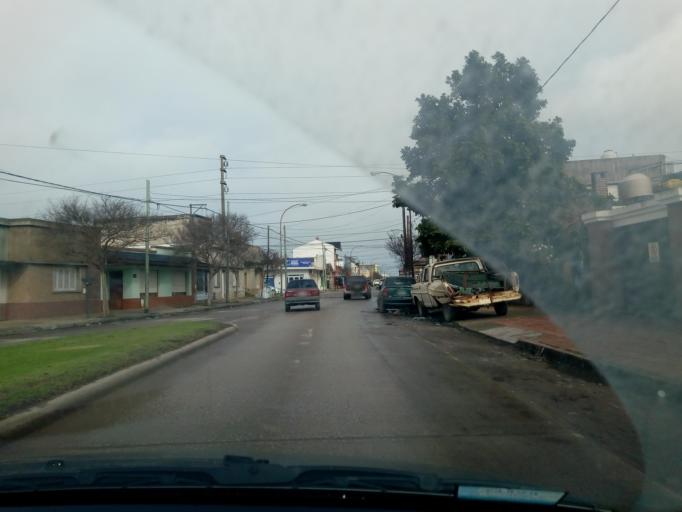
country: AR
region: Buenos Aires
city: Necochea
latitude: -38.5547
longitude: -58.7281
